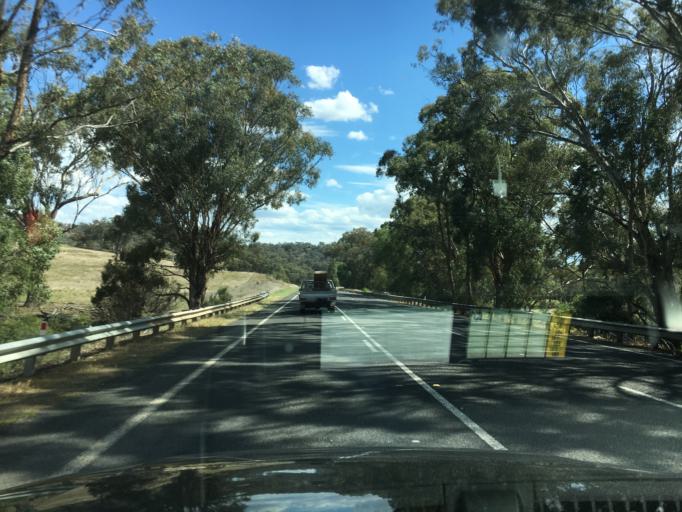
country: AU
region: New South Wales
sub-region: Liverpool Plains
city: Quirindi
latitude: -31.5169
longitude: 150.8525
